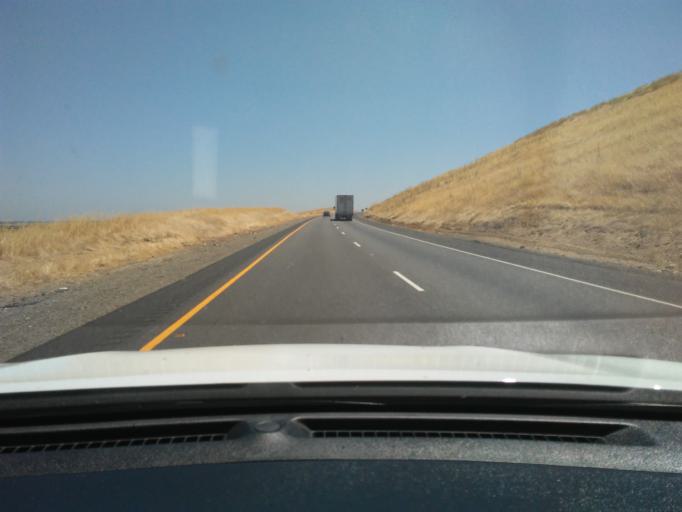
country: US
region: California
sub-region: Stanislaus County
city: Patterson
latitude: 37.4392
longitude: -121.1627
